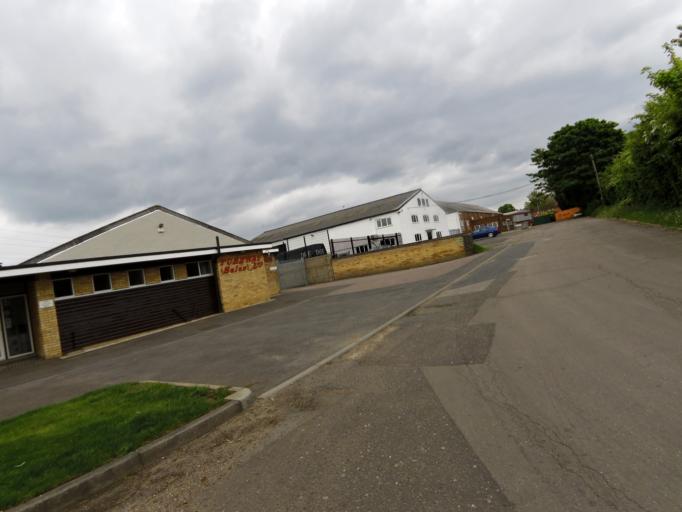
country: GB
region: England
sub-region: Suffolk
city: Bramford
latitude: 52.0594
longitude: 1.1235
